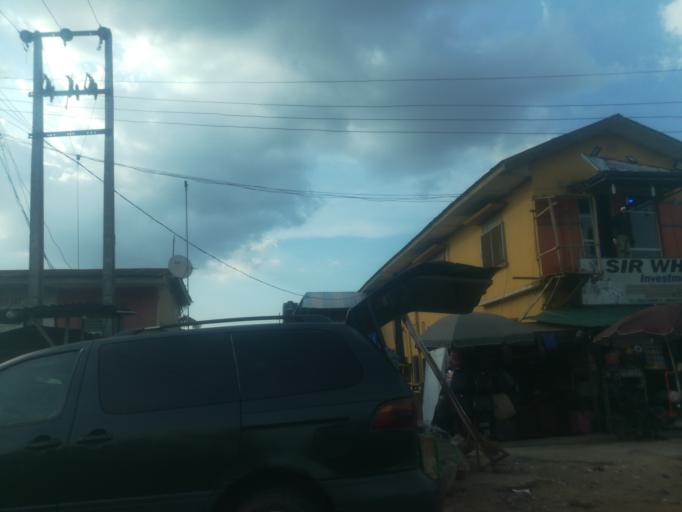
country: NG
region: Ogun
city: Abeokuta
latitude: 7.1341
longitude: 3.3307
